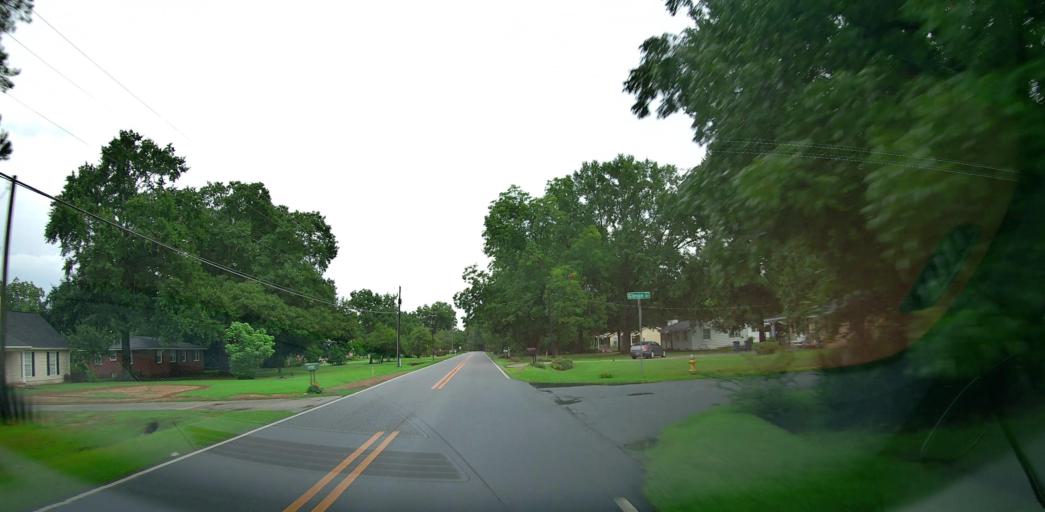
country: US
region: Georgia
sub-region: Peach County
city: Byron
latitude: 32.7337
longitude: -83.7040
